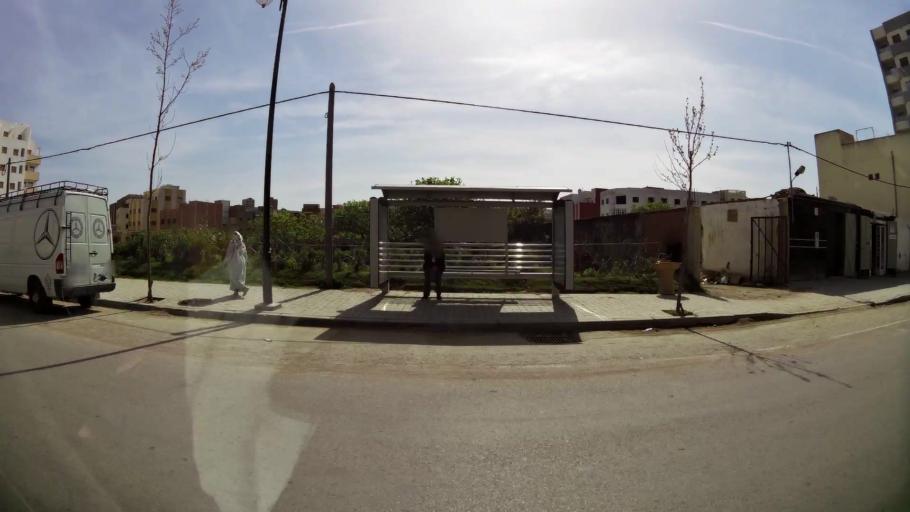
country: MA
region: Tanger-Tetouan
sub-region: Tanger-Assilah
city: Tangier
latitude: 35.7264
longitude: -5.8039
